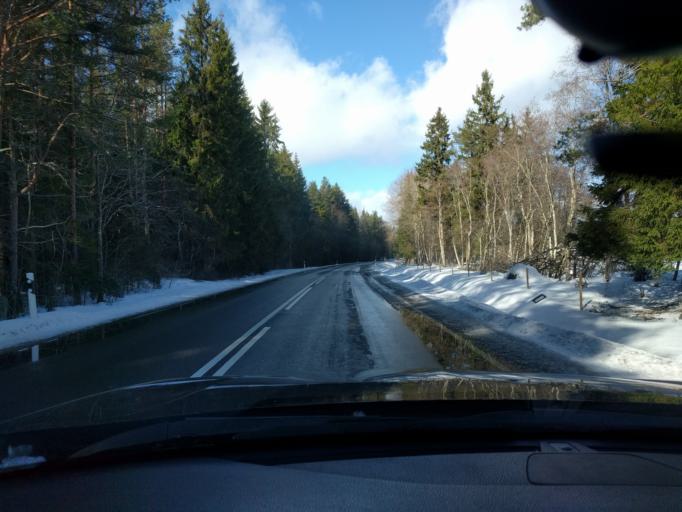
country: EE
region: Harju
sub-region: Raasiku vald
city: Raasiku
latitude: 59.2856
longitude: 25.1932
